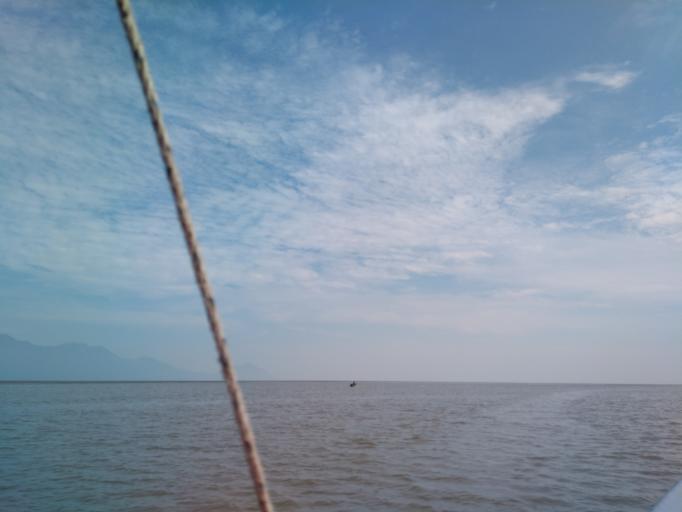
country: MY
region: Sarawak
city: Kuching
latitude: 1.6804
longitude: 110.4247
